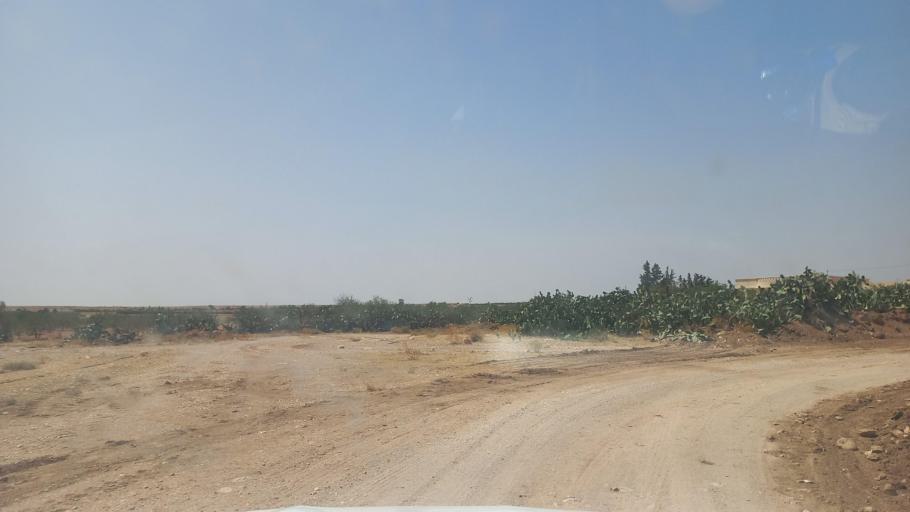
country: TN
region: Al Qasrayn
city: Kasserine
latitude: 35.2944
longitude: 8.9455
